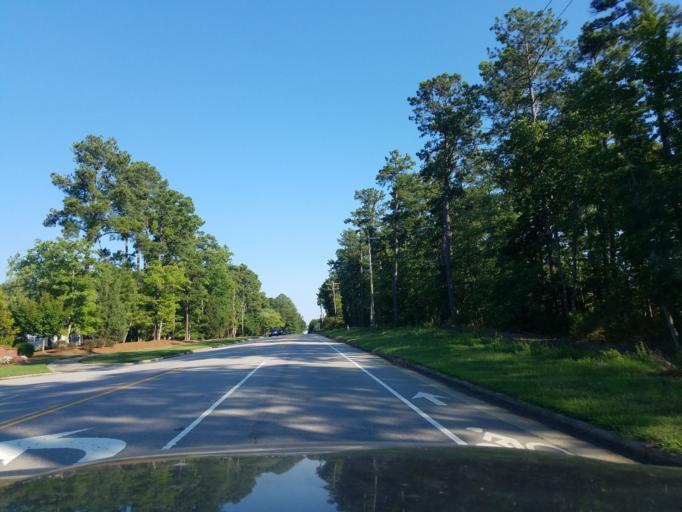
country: US
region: North Carolina
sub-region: Orange County
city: Chapel Hill
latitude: 35.8794
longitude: -78.9532
